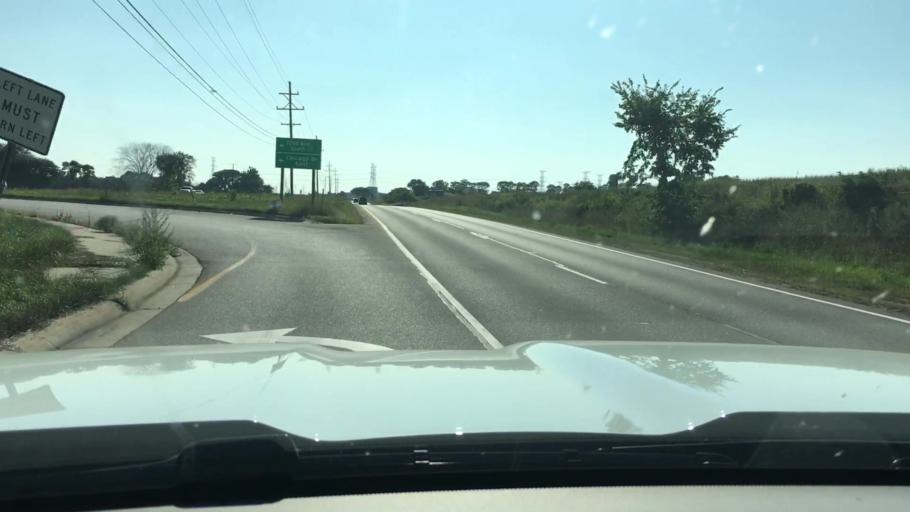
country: US
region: Michigan
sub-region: Ottawa County
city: Zeeland
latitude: 42.8326
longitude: -85.9617
